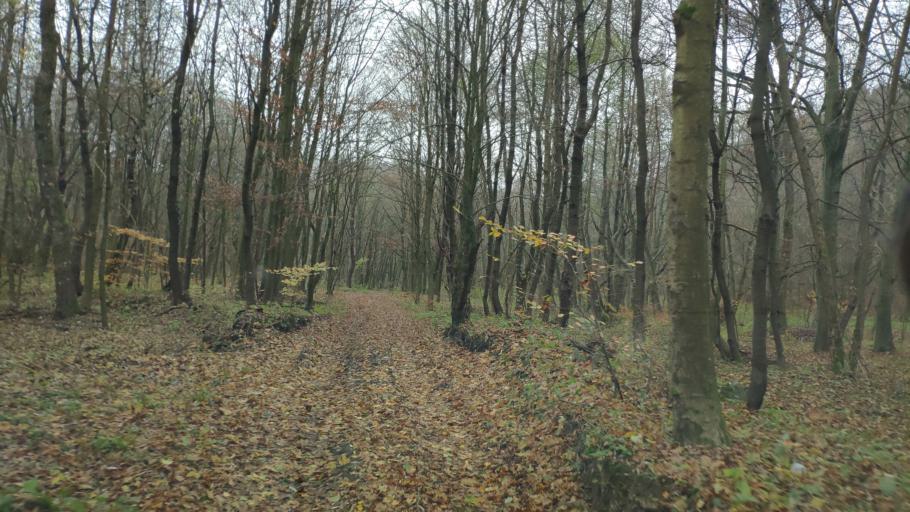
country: SK
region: Presovsky
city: Sabinov
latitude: 49.1429
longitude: 21.2146
